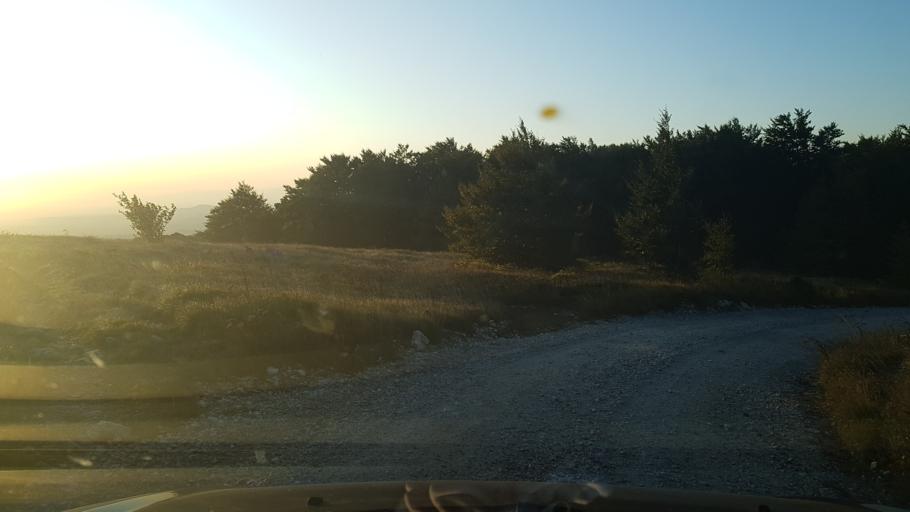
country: SI
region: Vipava
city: Vipava
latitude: 45.7727
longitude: 14.0503
